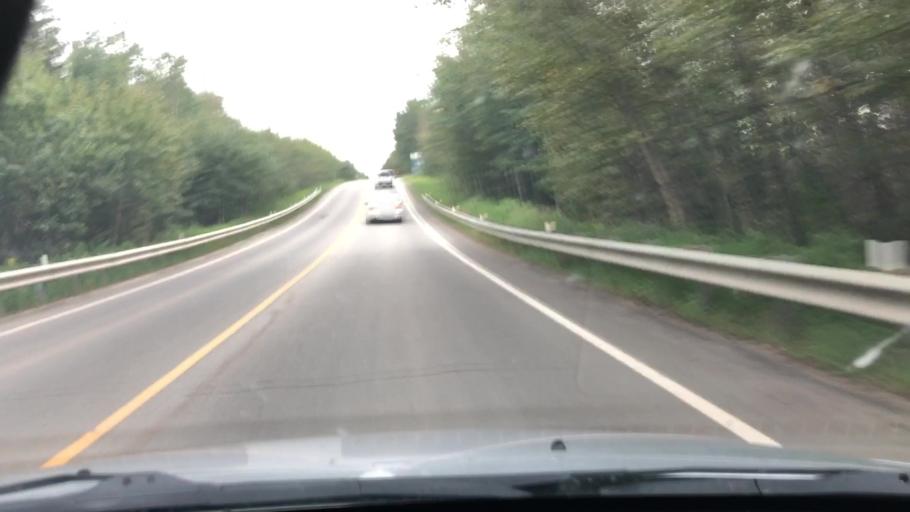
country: CA
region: Alberta
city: Devon
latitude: 53.4571
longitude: -113.6399
